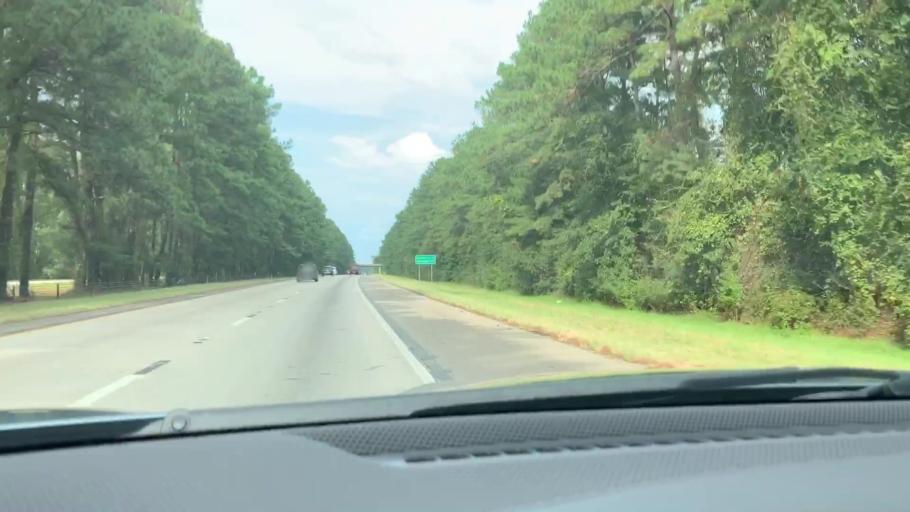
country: US
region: South Carolina
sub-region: Colleton County
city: Walterboro
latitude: 32.8914
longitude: -80.7117
